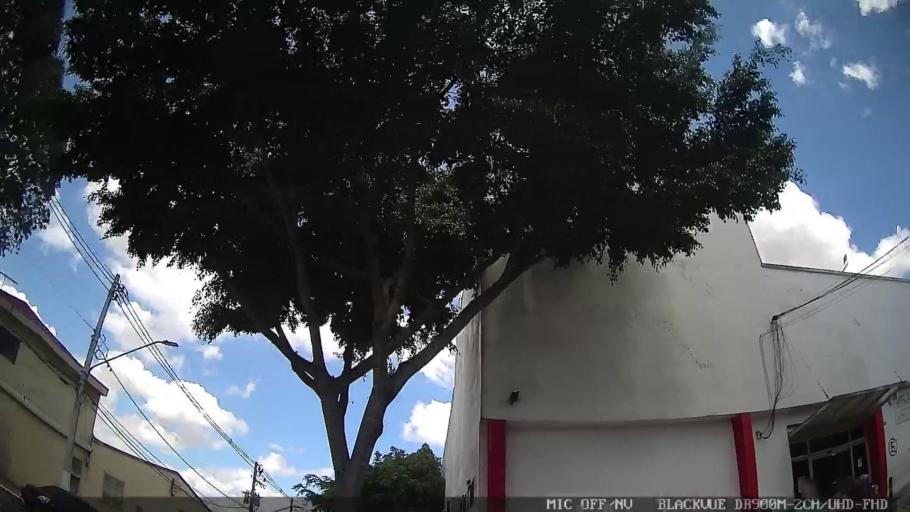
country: BR
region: Sao Paulo
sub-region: Diadema
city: Diadema
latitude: -23.6565
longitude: -46.6535
